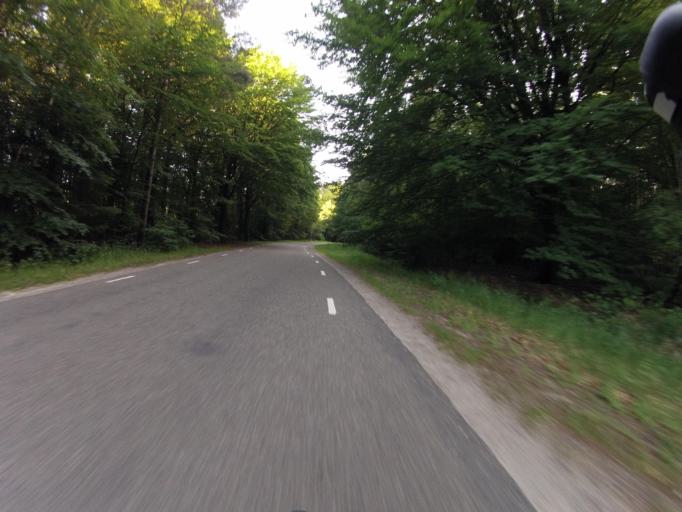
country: NL
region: Overijssel
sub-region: Gemeente Oldenzaal
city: Oldenzaal
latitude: 52.2981
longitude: 6.9645
